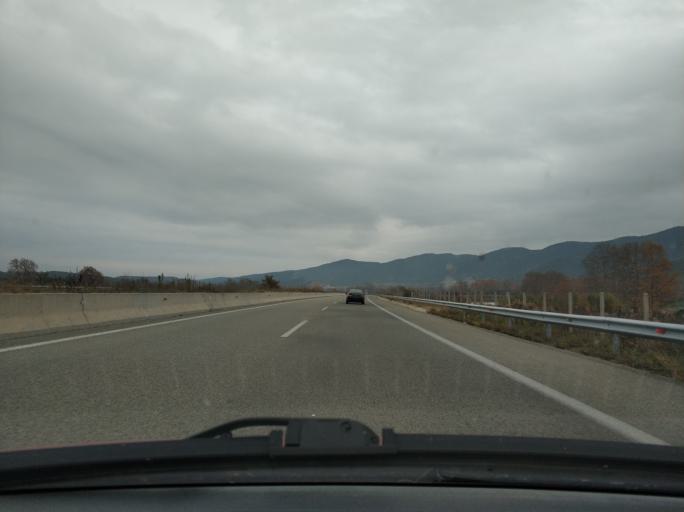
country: GR
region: East Macedonia and Thrace
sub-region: Nomos Kavalas
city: Eleftheres
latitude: 40.8769
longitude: 24.2126
